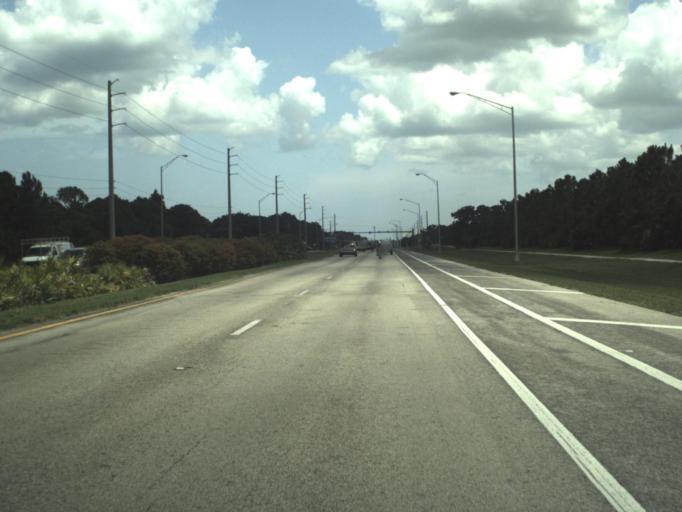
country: US
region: Florida
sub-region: Martin County
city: Port Salerno
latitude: 27.1135
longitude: -80.1744
